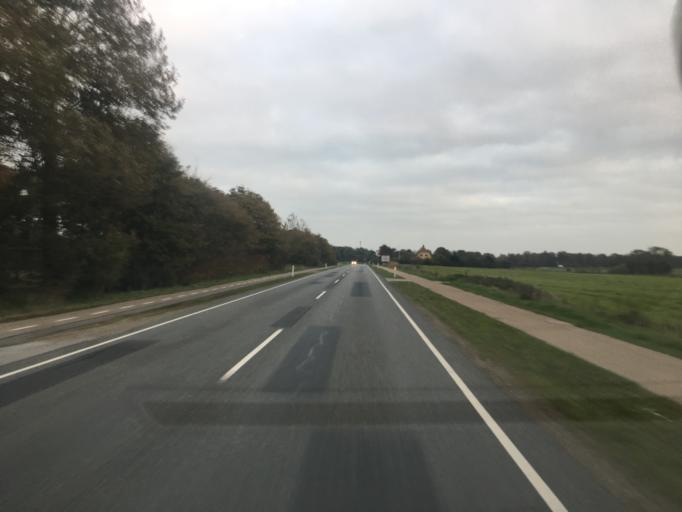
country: DK
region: South Denmark
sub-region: Tonder Kommune
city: Tonder
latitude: 54.9466
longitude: 8.8385
